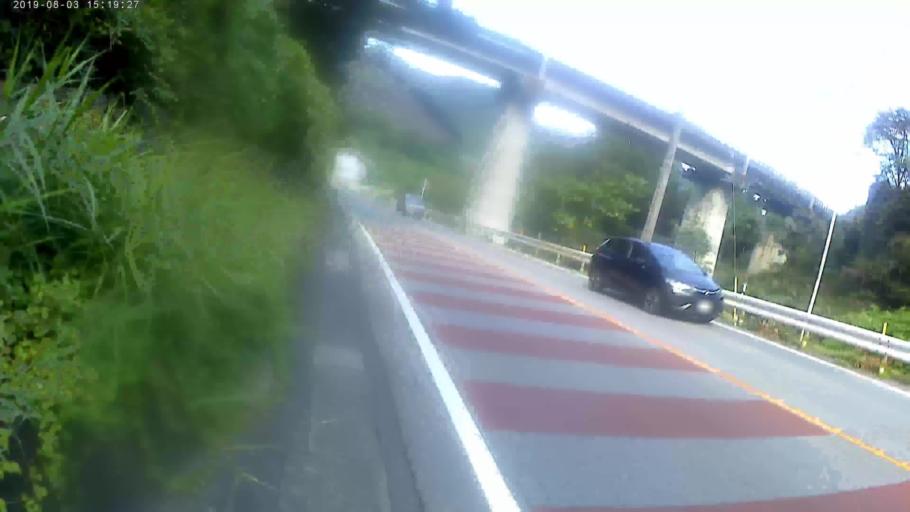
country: JP
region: Yamanashi
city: Otsuki
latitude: 35.6020
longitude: 138.8595
